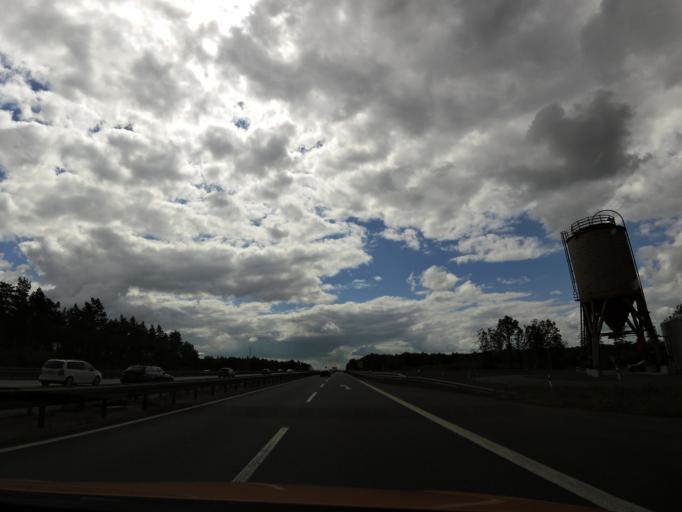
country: DE
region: Lower Saxony
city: Lehrte
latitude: 52.3997
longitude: 9.8991
